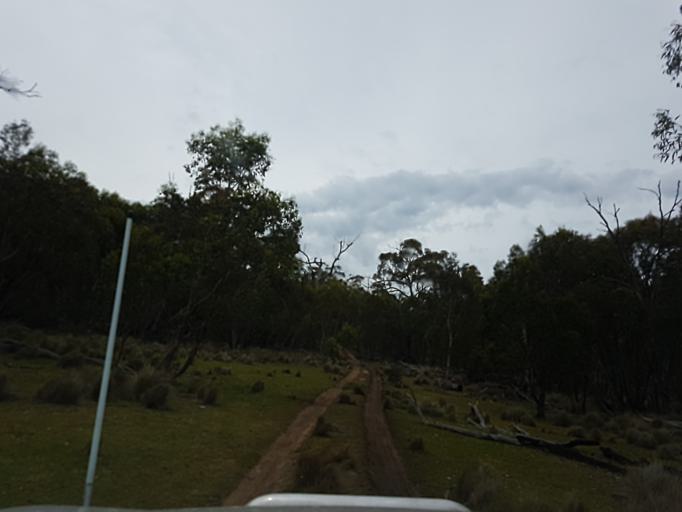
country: AU
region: New South Wales
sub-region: Snowy River
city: Jindabyne
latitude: -36.8530
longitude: 148.2592
